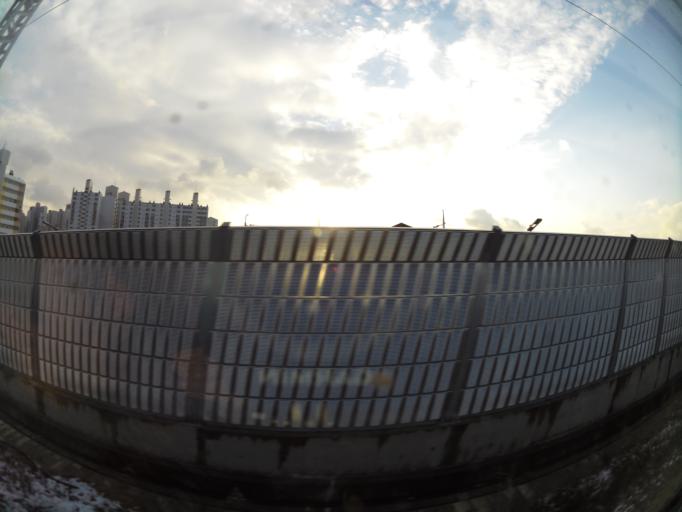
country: KR
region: Daejeon
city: Daejeon
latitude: 36.3451
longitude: 127.4244
